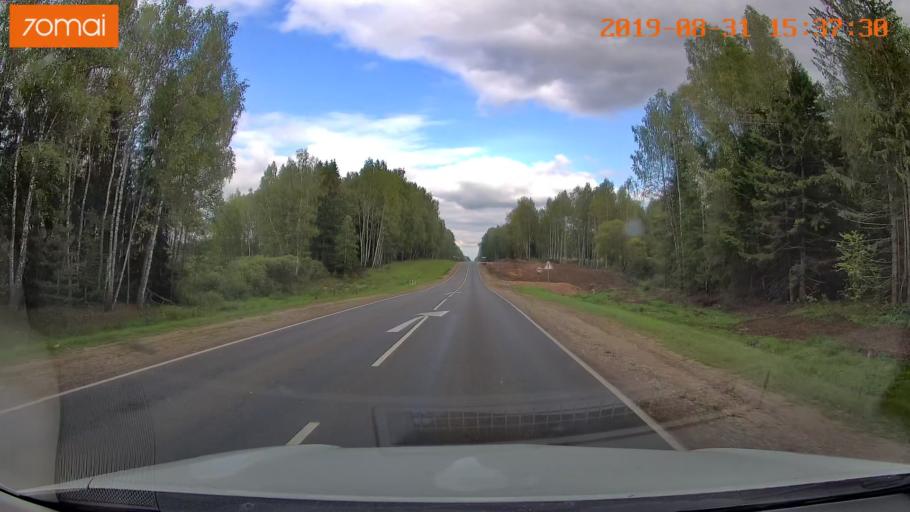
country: RU
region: Kaluga
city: Mosal'sk
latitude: 54.6187
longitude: 34.7859
